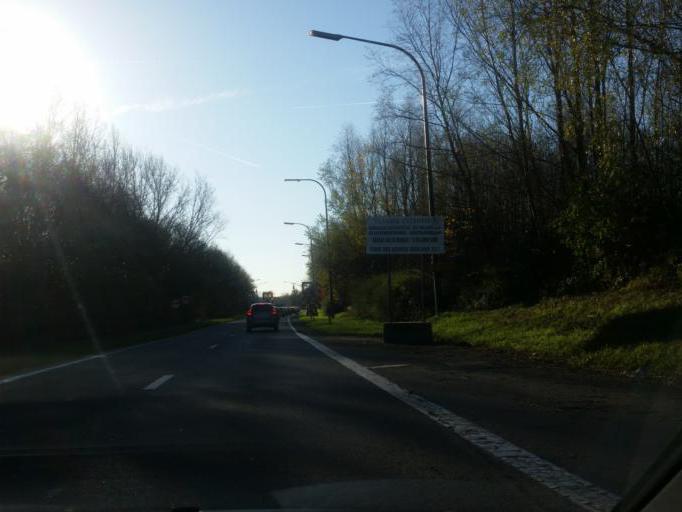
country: BE
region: Flanders
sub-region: Provincie Vlaams-Brabant
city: Zaventem
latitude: 50.8765
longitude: 4.4592
